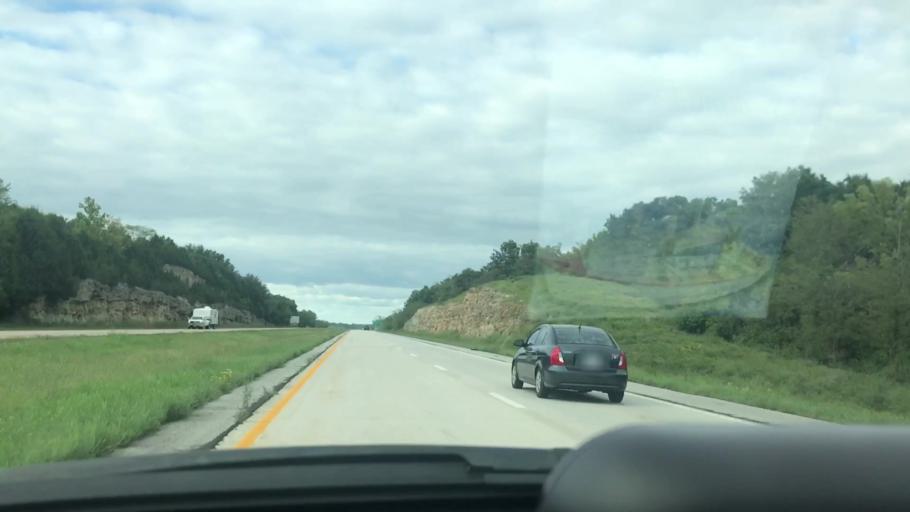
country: US
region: Missouri
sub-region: Benton County
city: Warsaw
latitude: 38.2725
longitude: -93.3657
